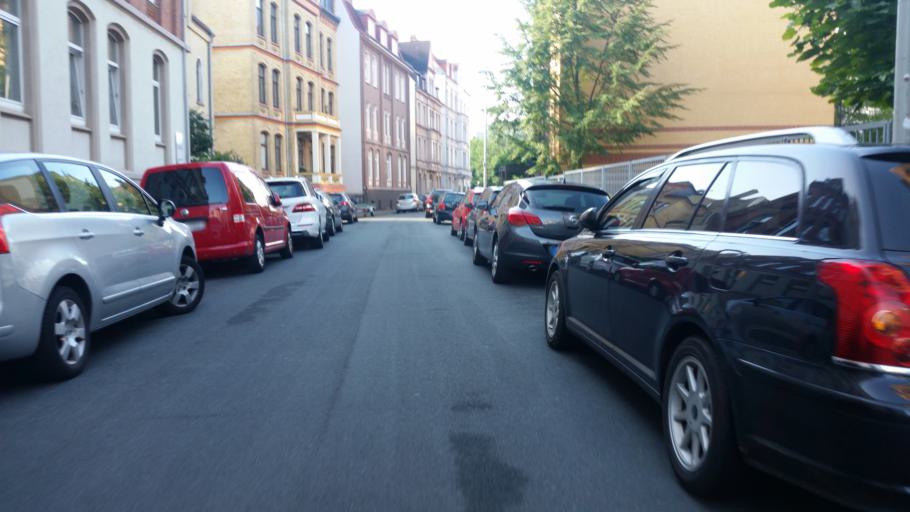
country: DE
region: Lower Saxony
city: Hannover
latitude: 52.3756
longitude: 9.7529
